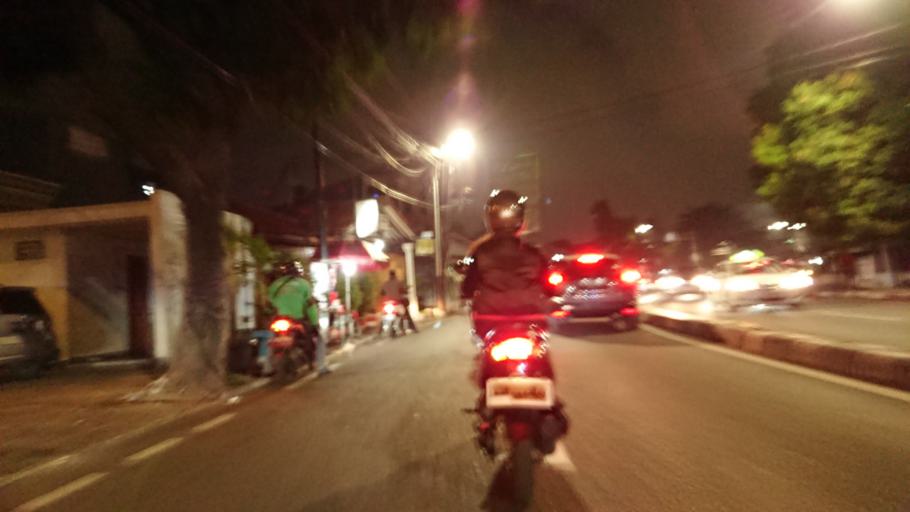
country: ID
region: Jakarta Raya
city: Jakarta
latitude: -6.1980
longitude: 106.8034
